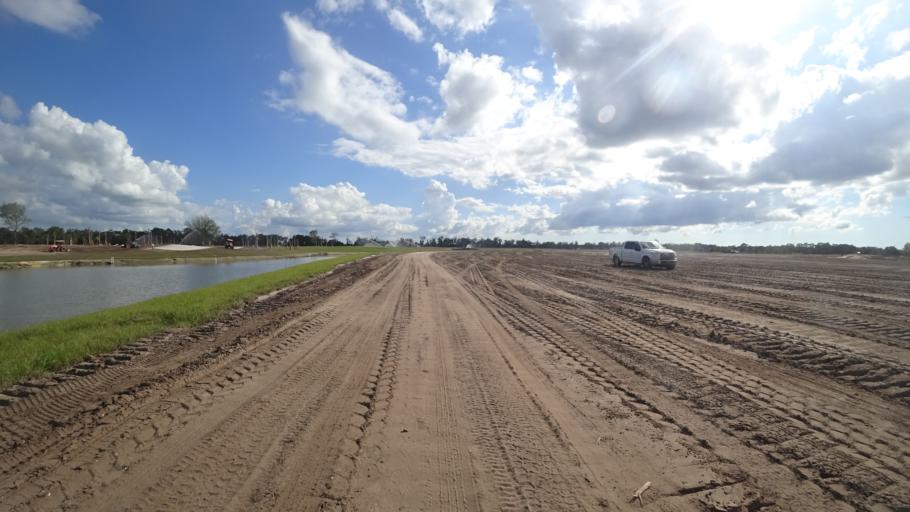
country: US
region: Florida
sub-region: Sarasota County
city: The Meadows
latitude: 27.4652
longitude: -82.3903
